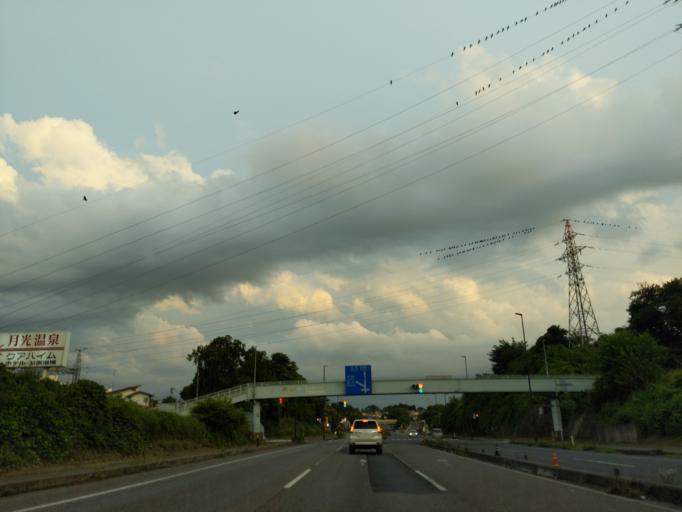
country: JP
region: Fukushima
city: Koriyama
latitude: 37.3518
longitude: 140.3555
